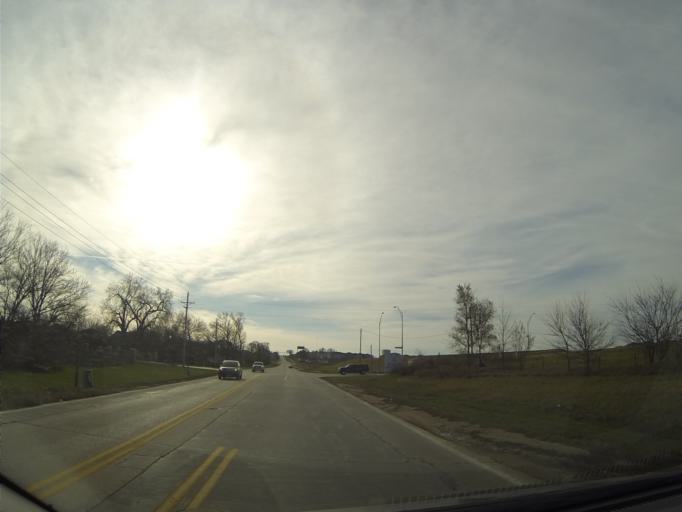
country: US
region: Nebraska
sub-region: Douglas County
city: Elkhorn
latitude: 41.2748
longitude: -96.2158
